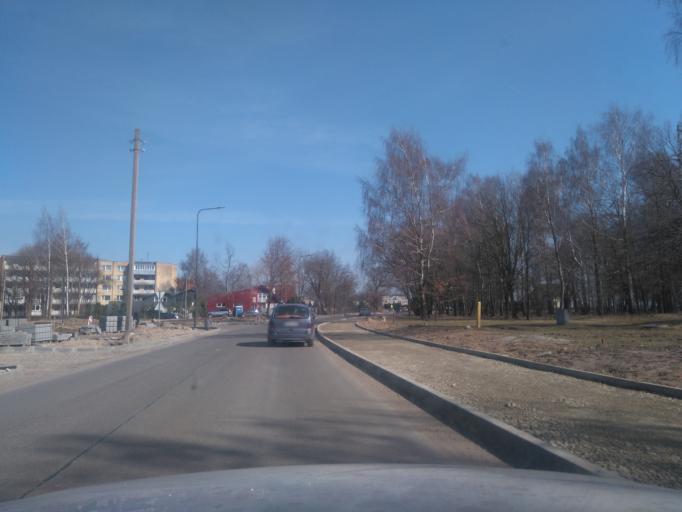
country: LT
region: Kauno apskritis
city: Dainava (Kaunas)
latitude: 54.8854
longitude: 23.9515
